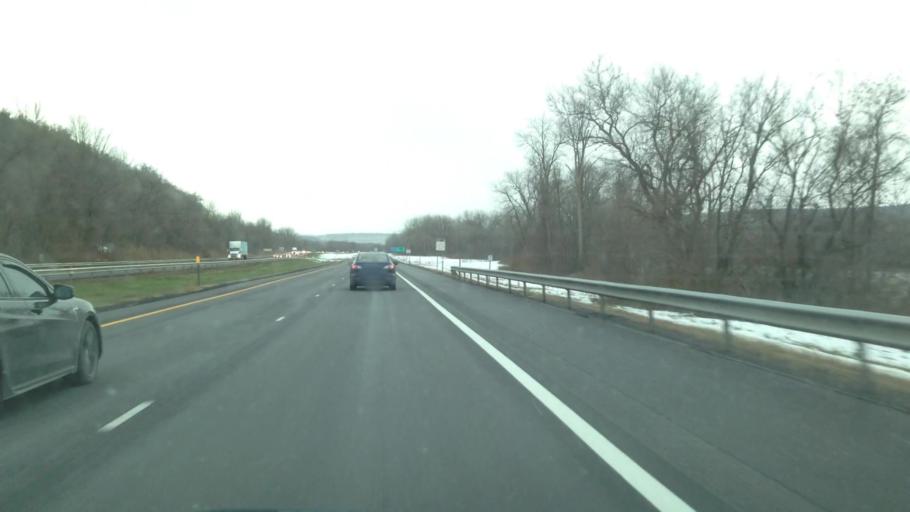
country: US
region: New York
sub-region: Montgomery County
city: Fonda
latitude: 42.9389
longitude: -74.4052
